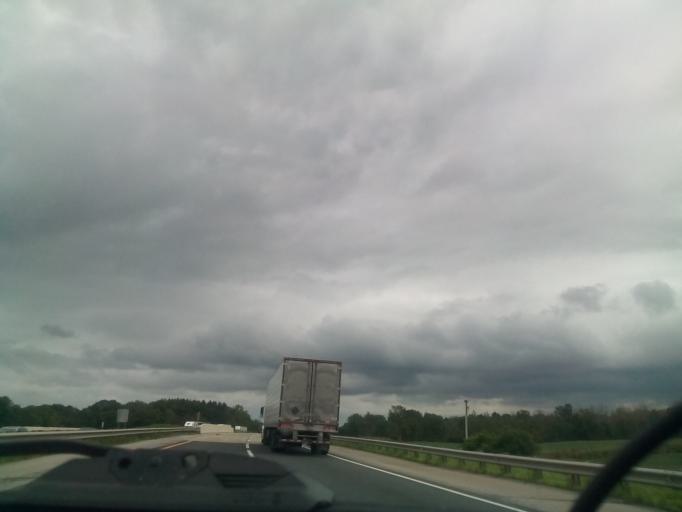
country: US
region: Indiana
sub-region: Steuben County
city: Fremont
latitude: 41.6599
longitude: -84.8452
